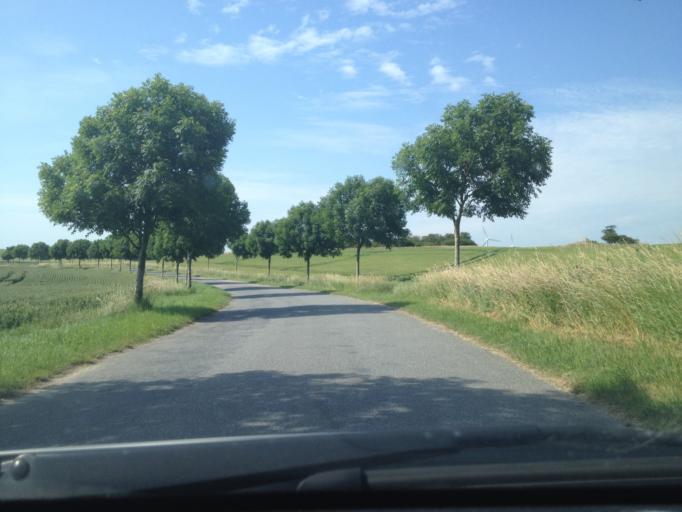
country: DK
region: Central Jutland
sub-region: Samso Kommune
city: Tranebjerg
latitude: 55.7863
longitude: 10.5816
